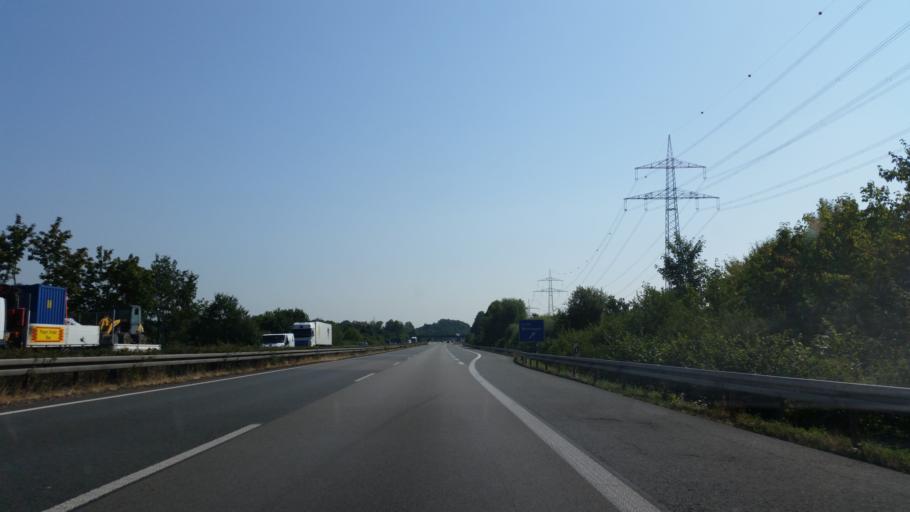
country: DE
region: North Rhine-Westphalia
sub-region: Regierungsbezirk Munster
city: Lotte
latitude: 52.2648
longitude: 7.8857
